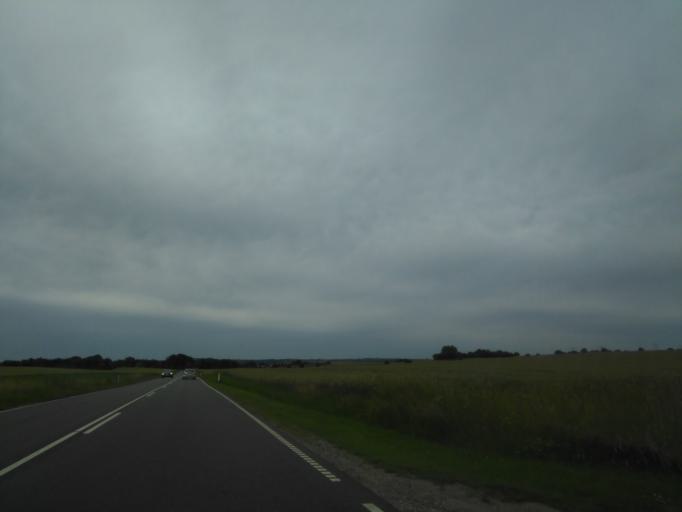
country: DK
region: Central Jutland
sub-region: Arhus Kommune
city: Solbjerg
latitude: 56.0199
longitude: 10.0442
